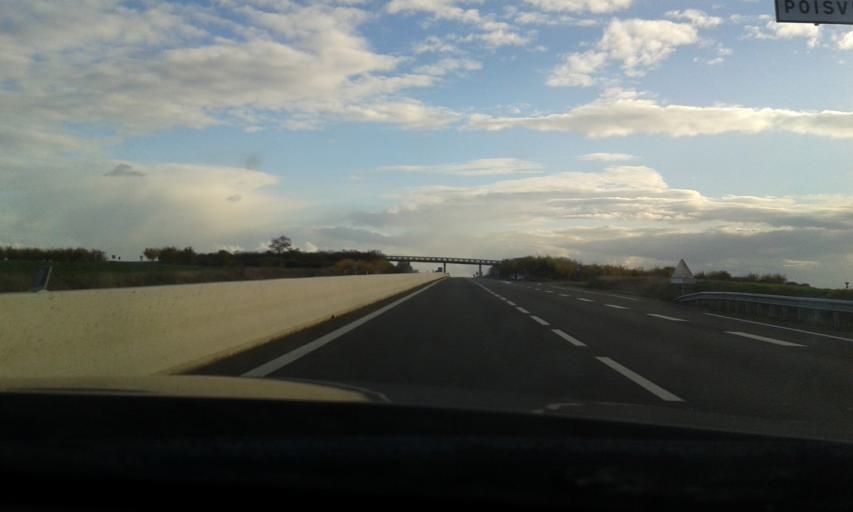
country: FR
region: Centre
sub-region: Departement d'Eure-et-Loir
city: Leves
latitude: 48.5101
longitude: 1.4623
